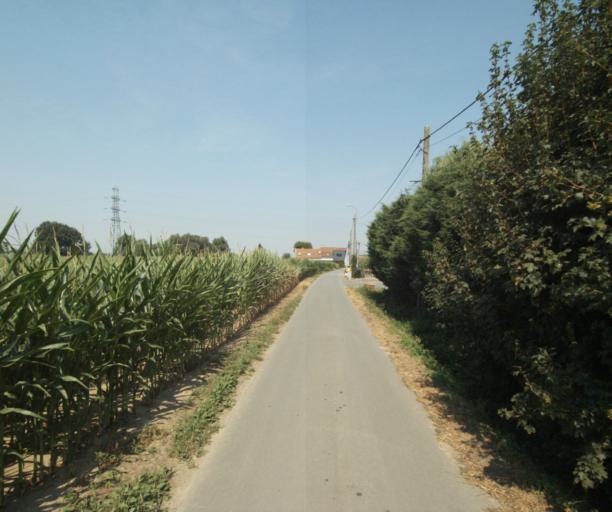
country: FR
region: Nord-Pas-de-Calais
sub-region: Departement du Nord
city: Wambrechies
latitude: 50.6826
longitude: 3.0303
